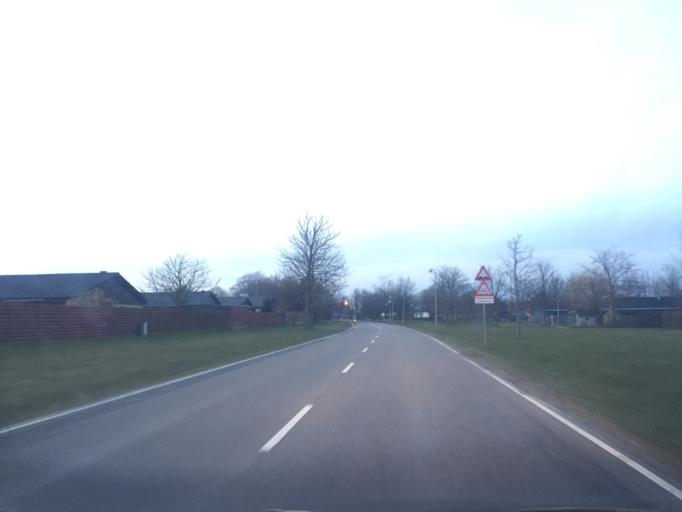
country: DK
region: Capital Region
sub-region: Hoje-Taastrup Kommune
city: Taastrup
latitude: 55.6408
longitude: 12.3089
